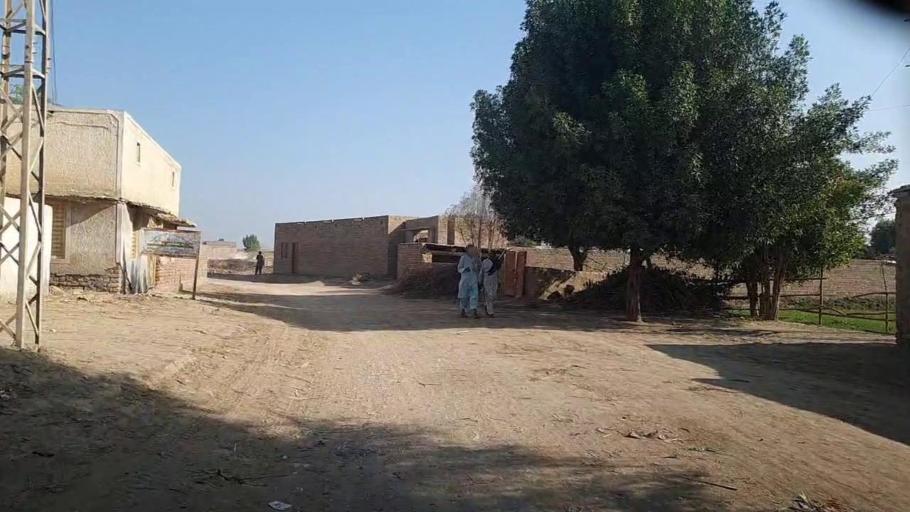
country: PK
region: Sindh
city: Darya Khan Marri
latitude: 26.6722
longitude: 68.3202
